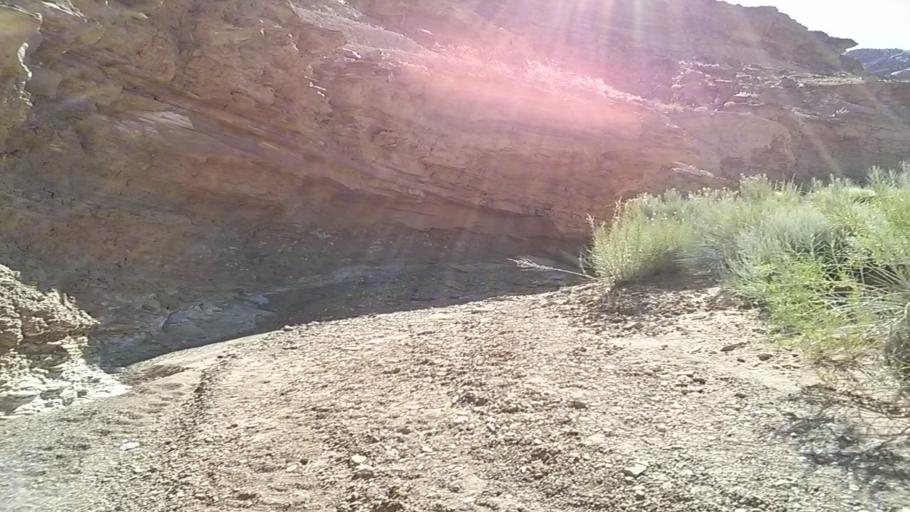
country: US
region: Utah
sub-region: Grand County
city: Moab
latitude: 38.4453
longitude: -109.9562
